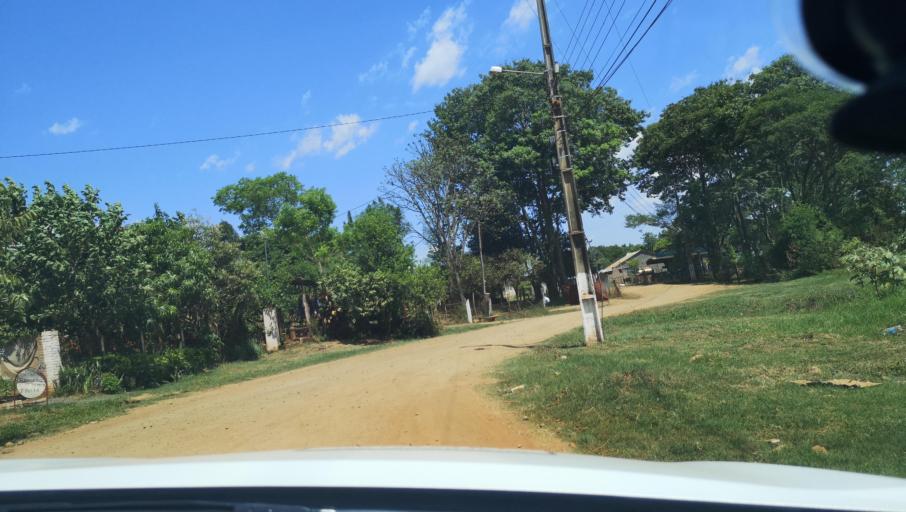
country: PY
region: Itapua
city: Carmen del Parana
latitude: -27.1619
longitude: -56.2290
